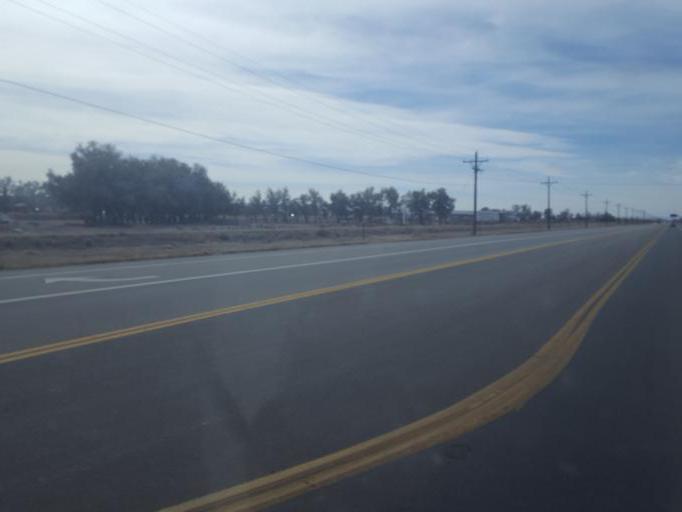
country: US
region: Colorado
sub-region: Alamosa County
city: Alamosa
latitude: 37.4502
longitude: -105.8802
